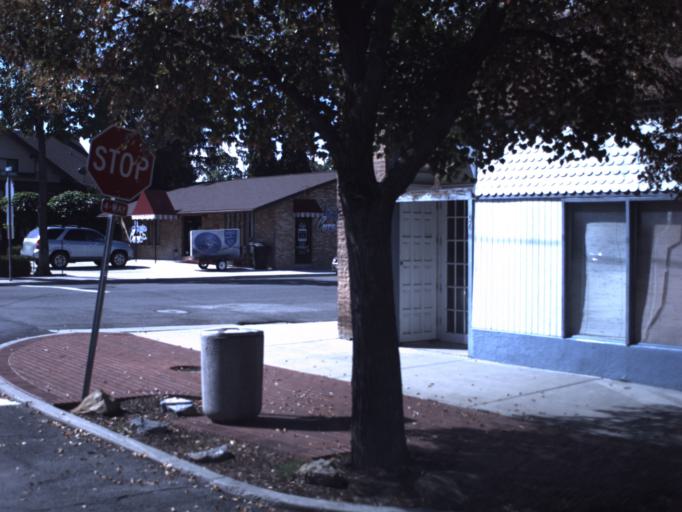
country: US
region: Utah
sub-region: Utah County
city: Payson
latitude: 40.0427
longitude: -111.7323
